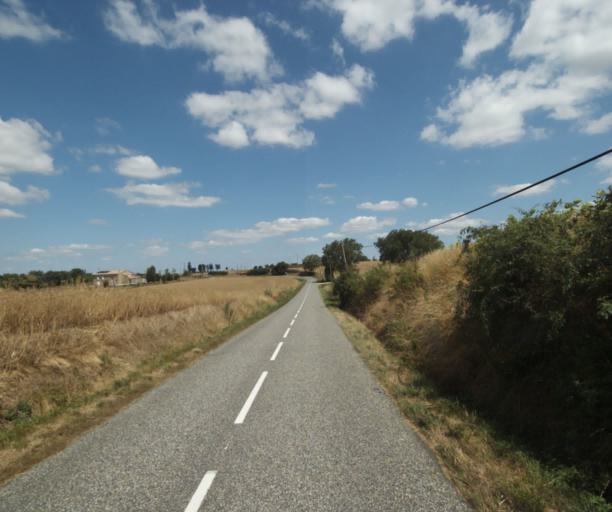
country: FR
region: Midi-Pyrenees
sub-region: Departement de la Haute-Garonne
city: Saint-Felix-Lauragais
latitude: 43.4653
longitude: 1.8340
